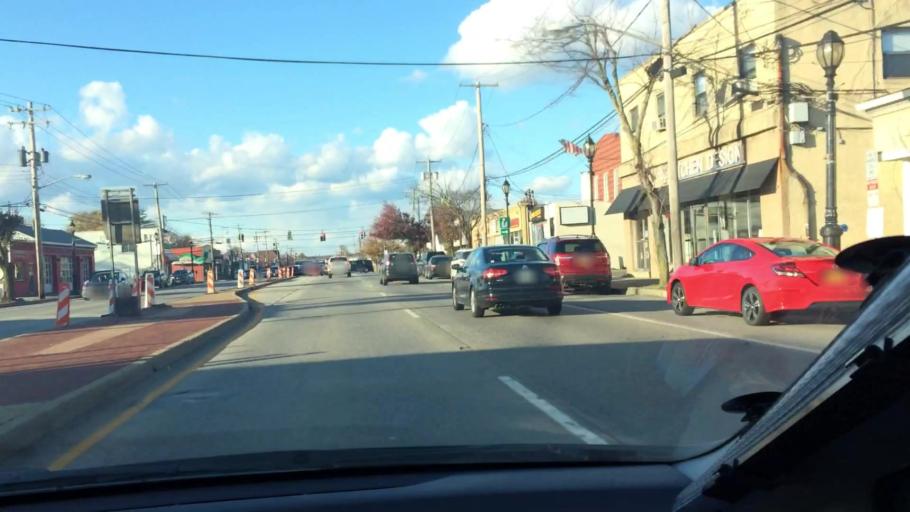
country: US
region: New York
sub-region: Suffolk County
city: Deer Park
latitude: 40.7580
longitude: -73.3277
